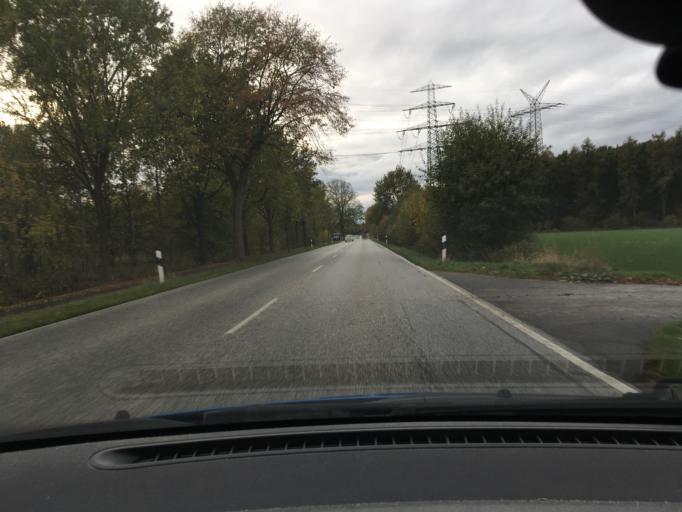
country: DE
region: Schleswig-Holstein
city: Bornsen
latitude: 53.4876
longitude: 10.3021
